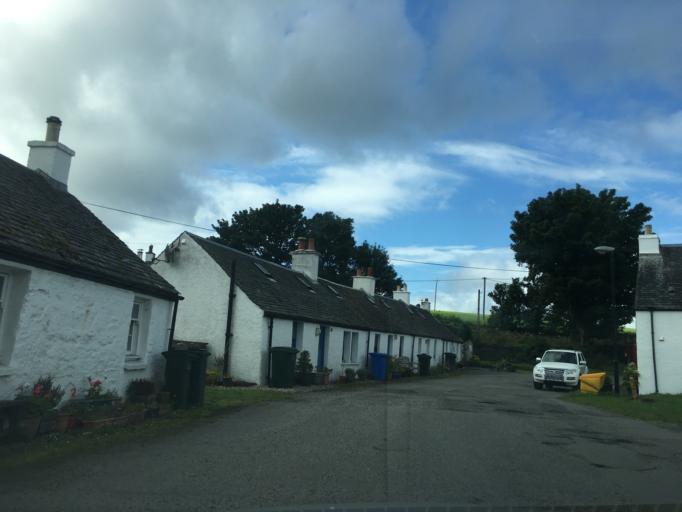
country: GB
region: Scotland
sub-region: Argyll and Bute
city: Oban
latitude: 56.2177
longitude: -5.6321
